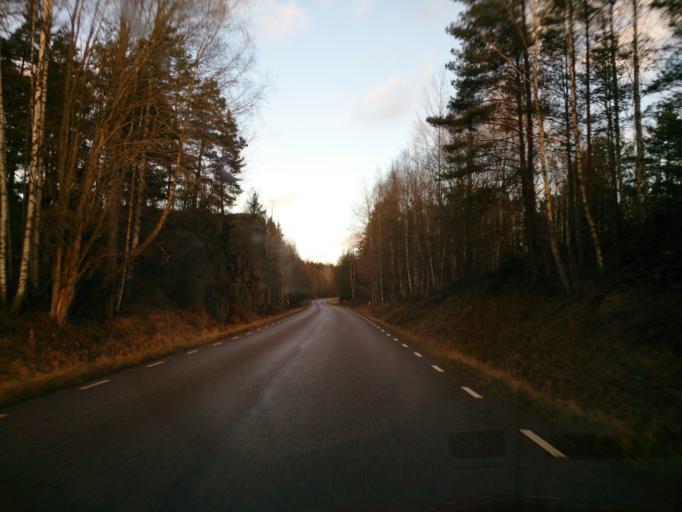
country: SE
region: OEstergoetland
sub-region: Atvidabergs Kommun
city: Atvidaberg
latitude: 58.2449
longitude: 16.0114
